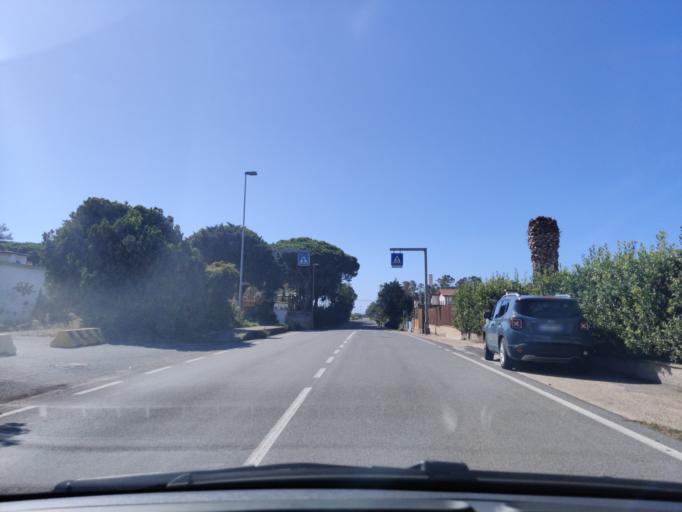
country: IT
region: Latium
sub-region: Citta metropolitana di Roma Capitale
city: Aurelia
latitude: 42.1397
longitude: 11.7840
